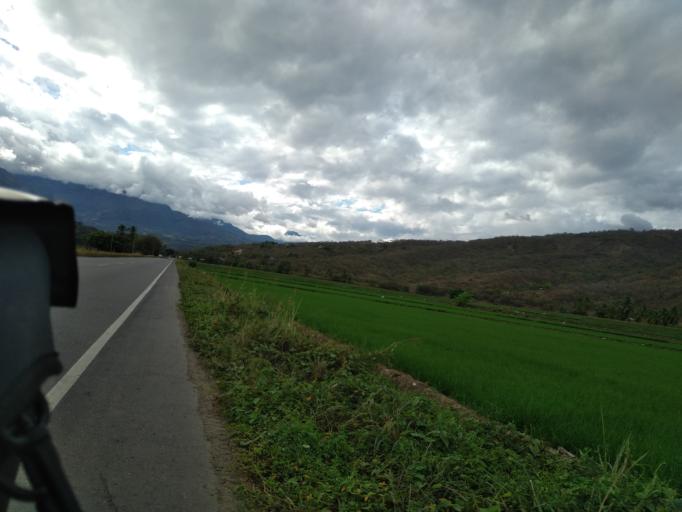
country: PE
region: Amazonas
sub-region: Utcubamba
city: Jamalca
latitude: -5.8192
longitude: -78.2855
